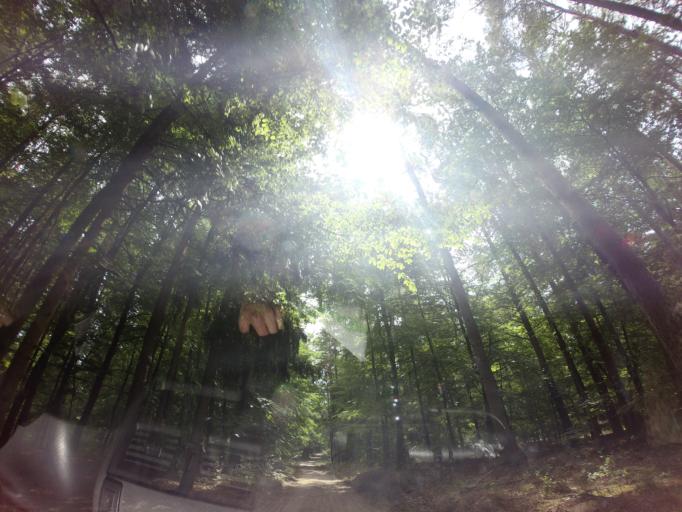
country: PL
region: West Pomeranian Voivodeship
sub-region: Powiat choszczenski
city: Drawno
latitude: 53.1893
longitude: 15.7716
